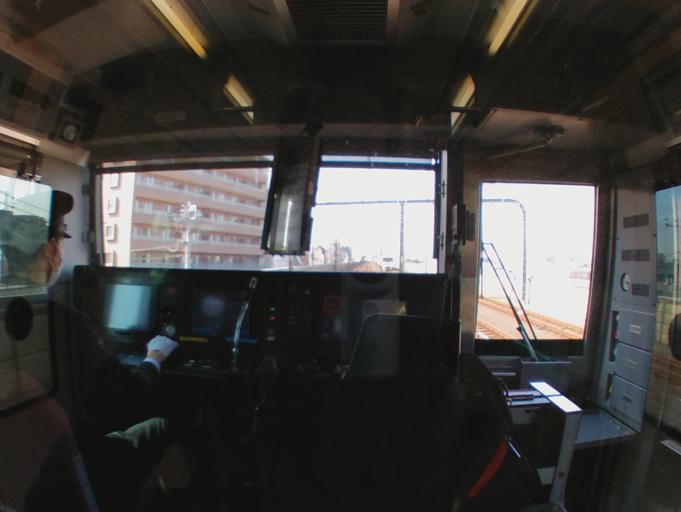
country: JP
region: Tokyo
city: Tokyo
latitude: 35.6503
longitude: 139.6337
